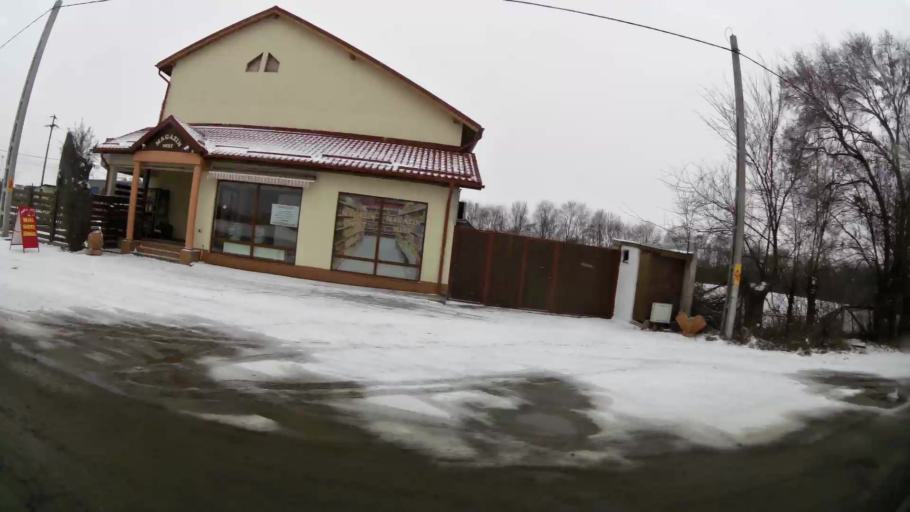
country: RO
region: Dambovita
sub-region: Comuna Ulmi
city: Ulmi
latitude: 44.8956
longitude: 25.5096
